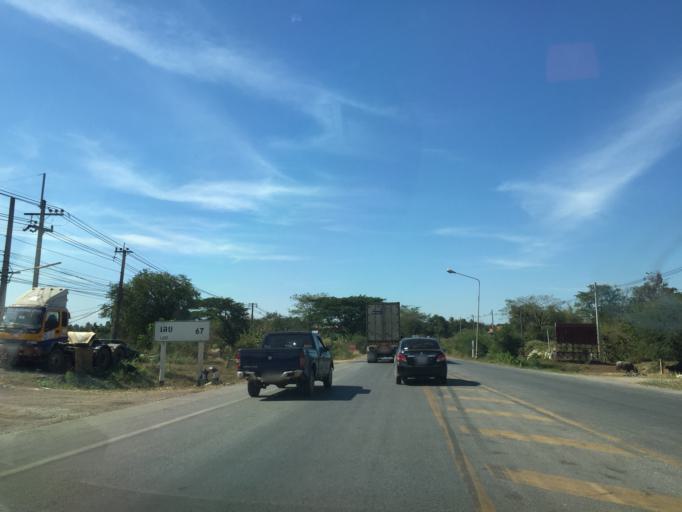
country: TH
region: Changwat Nong Bua Lamphu
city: Na Klang
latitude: 17.3100
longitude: 102.1775
